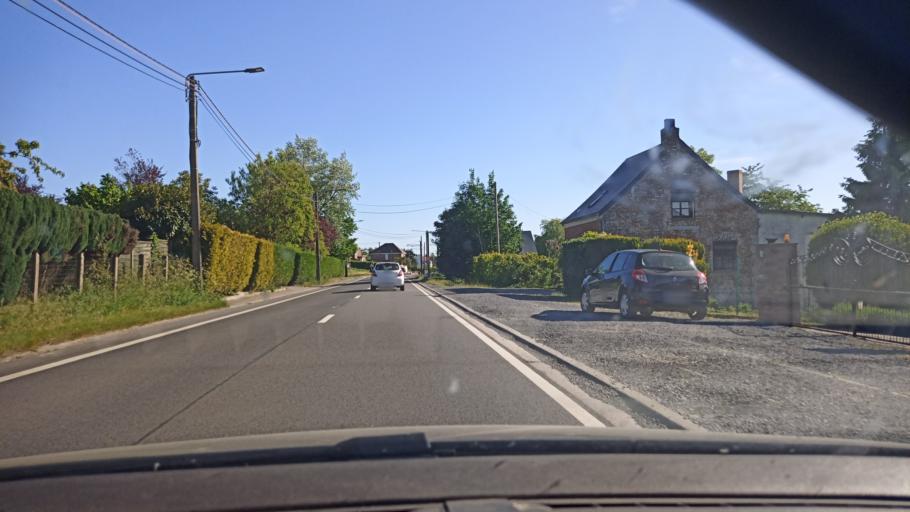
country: BE
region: Wallonia
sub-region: Province du Hainaut
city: Lobbes
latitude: 50.3619
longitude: 4.2726
